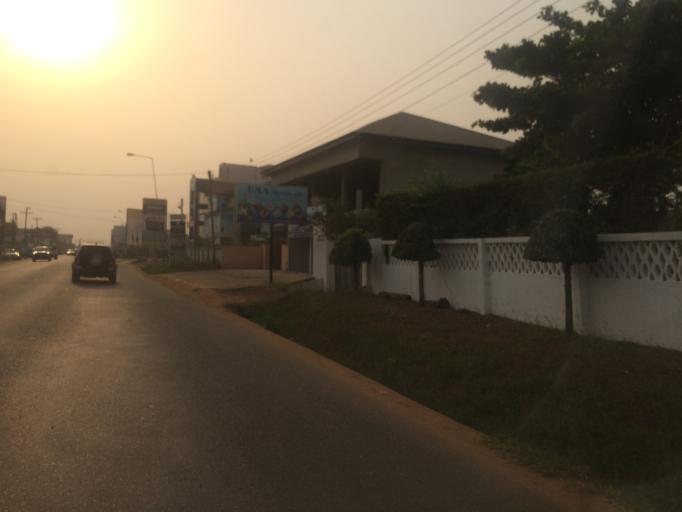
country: GH
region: Greater Accra
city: Nungua
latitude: 5.6358
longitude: -0.1021
